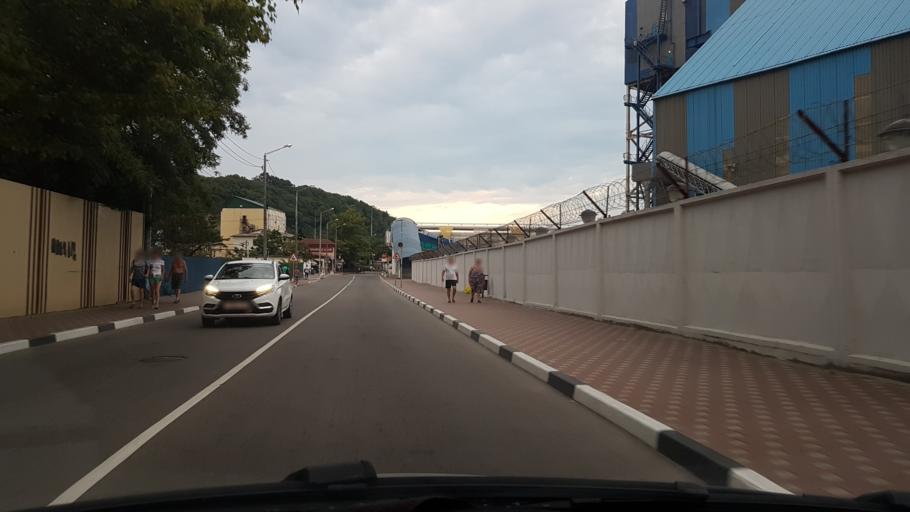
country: RU
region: Krasnodarskiy
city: Tuapse
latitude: 44.0934
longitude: 39.0795
